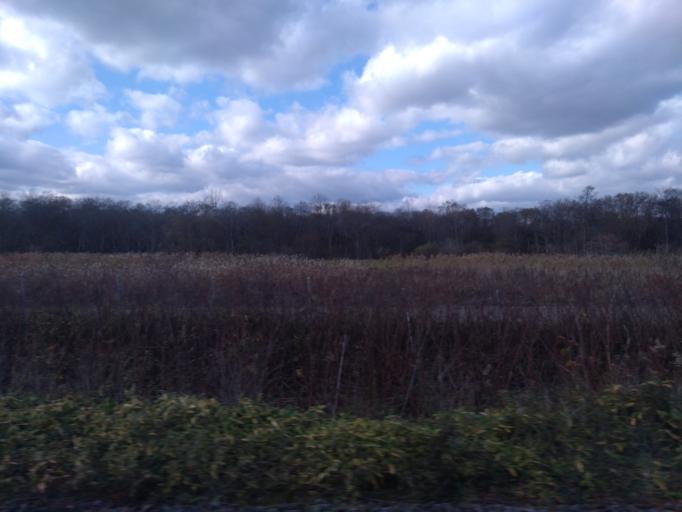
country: JP
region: Hokkaido
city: Shiraoi
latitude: 42.5046
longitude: 141.2793
